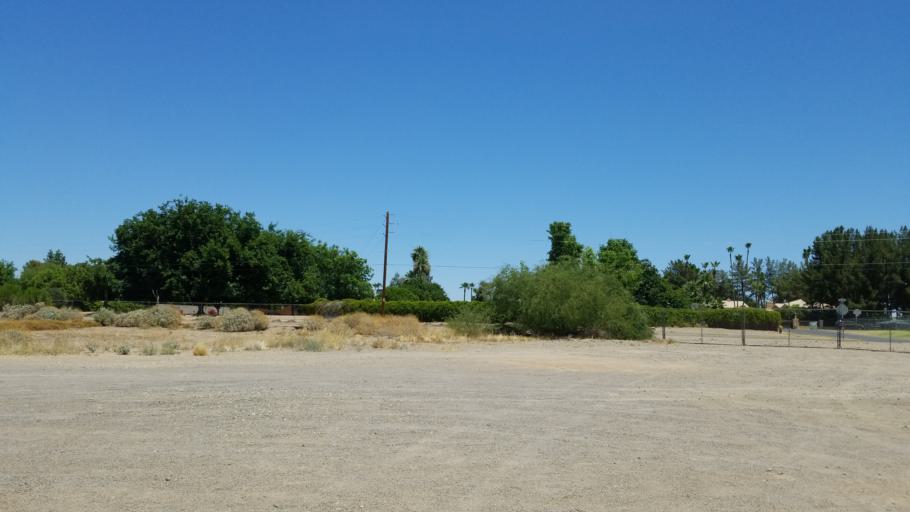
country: US
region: Arizona
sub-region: Maricopa County
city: Litchfield Park
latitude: 33.5125
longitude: -112.2909
